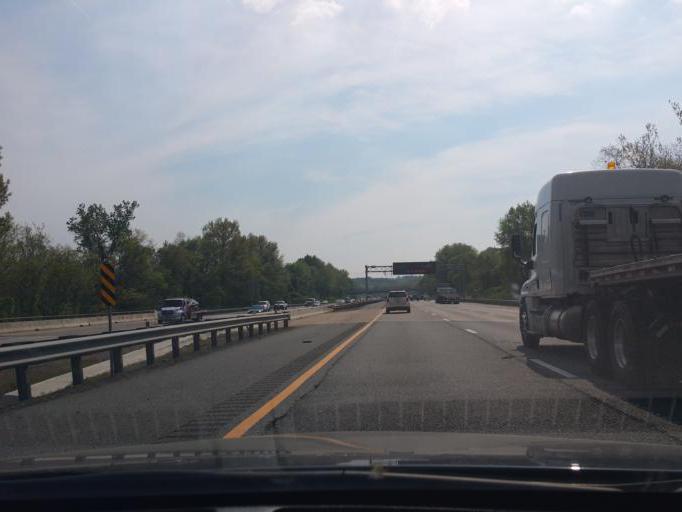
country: US
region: Maryland
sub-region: Harford County
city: Riverside
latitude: 39.4809
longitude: -76.2614
